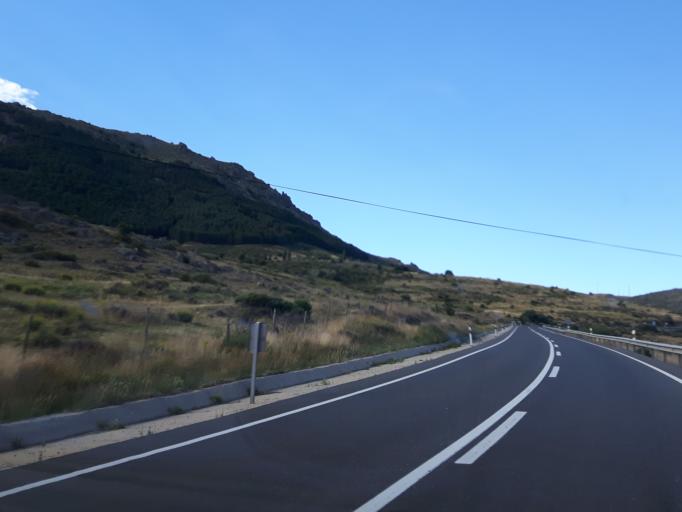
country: ES
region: Castille and Leon
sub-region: Provincia de Avila
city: Mengamunoz
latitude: 40.4940
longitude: -5.0052
